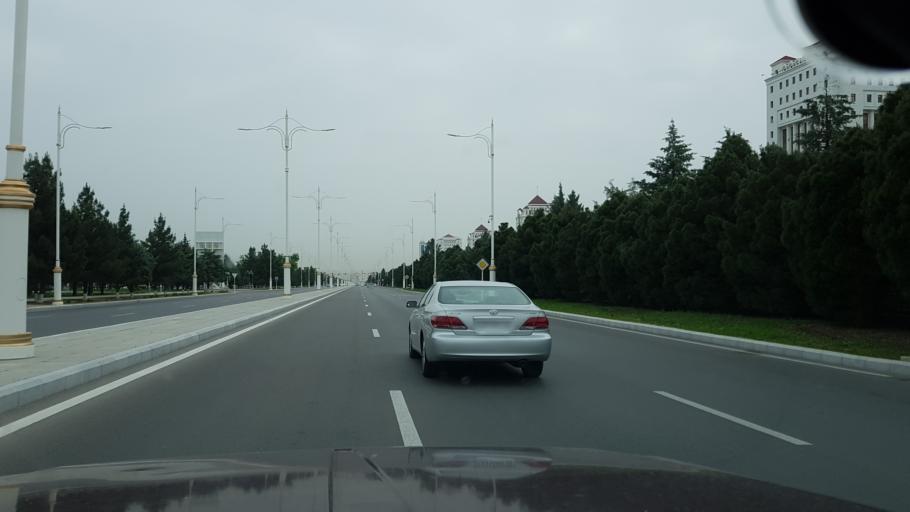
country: TM
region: Ahal
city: Ashgabat
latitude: 37.8817
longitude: 58.3874
